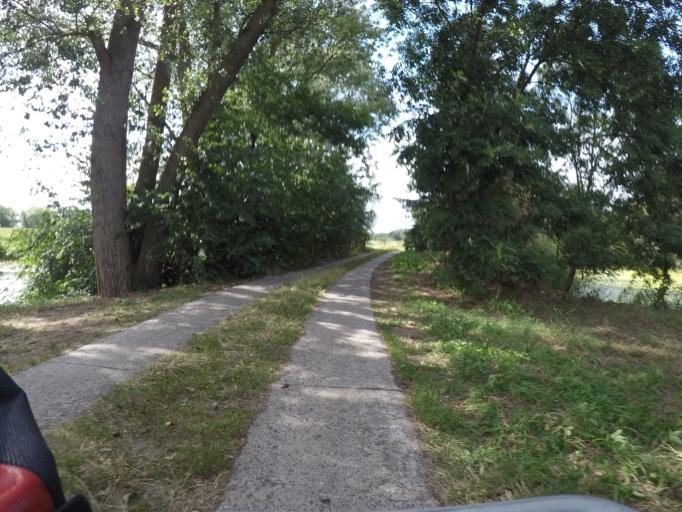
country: DE
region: Lower Saxony
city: Radbruch
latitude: 53.3663
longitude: 10.2804
